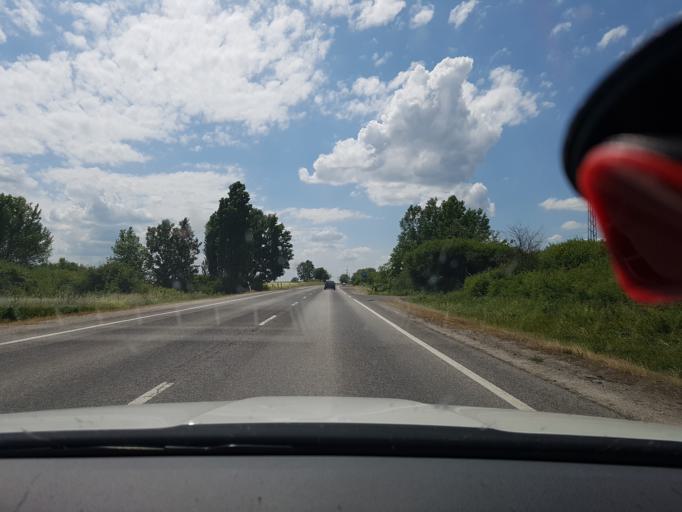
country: HU
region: Heves
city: Domoszlo
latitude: 47.7450
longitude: 20.1449
